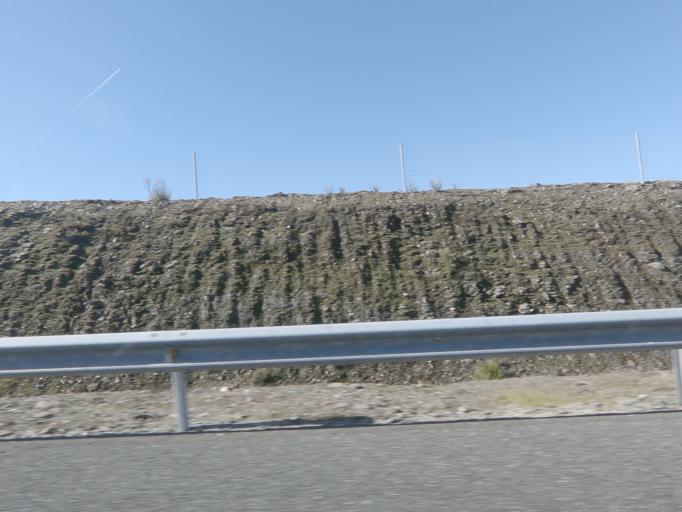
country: ES
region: Galicia
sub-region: Provincia de Pontevedra
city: Dozon
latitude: 42.5921
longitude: -8.0845
